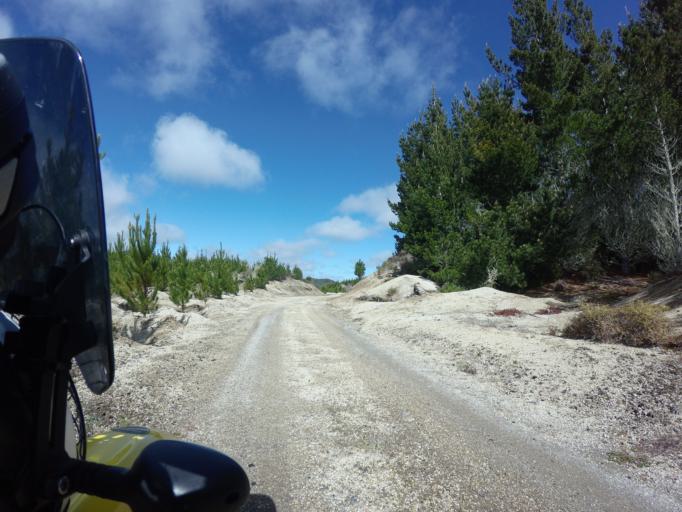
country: NZ
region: Bay of Plenty
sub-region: Whakatane District
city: Murupara
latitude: -38.8247
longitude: 176.5496
